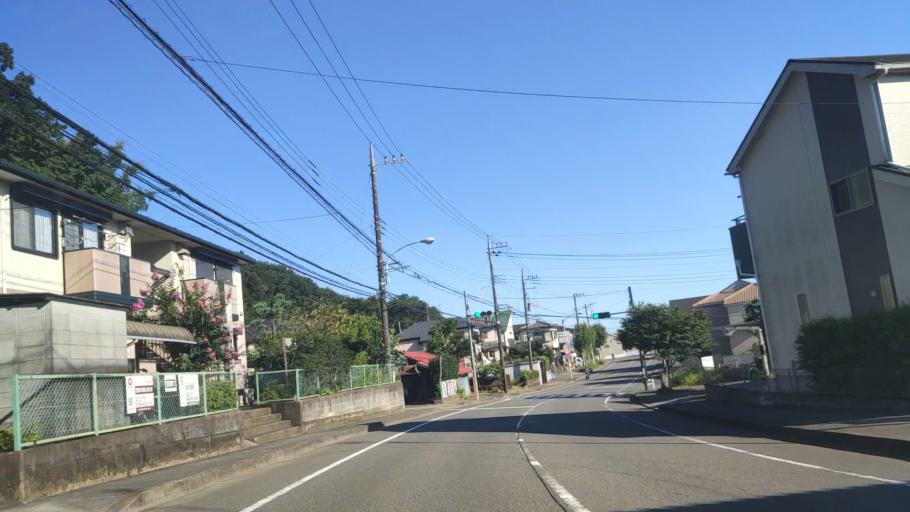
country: JP
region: Tokyo
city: Hachioji
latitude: 35.6088
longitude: 139.3140
